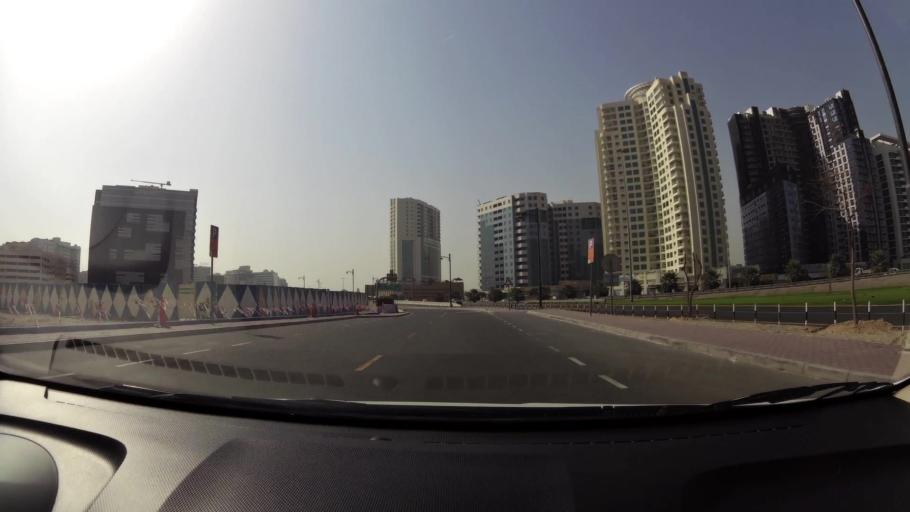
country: AE
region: Ash Shariqah
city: Sharjah
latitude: 25.2905
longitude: 55.3623
